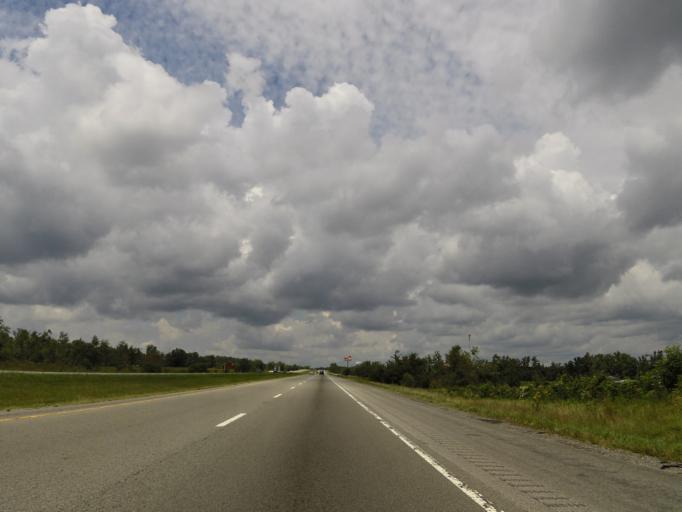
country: US
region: Tennessee
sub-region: Putnam County
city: Monterey
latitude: 36.0937
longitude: -85.2301
